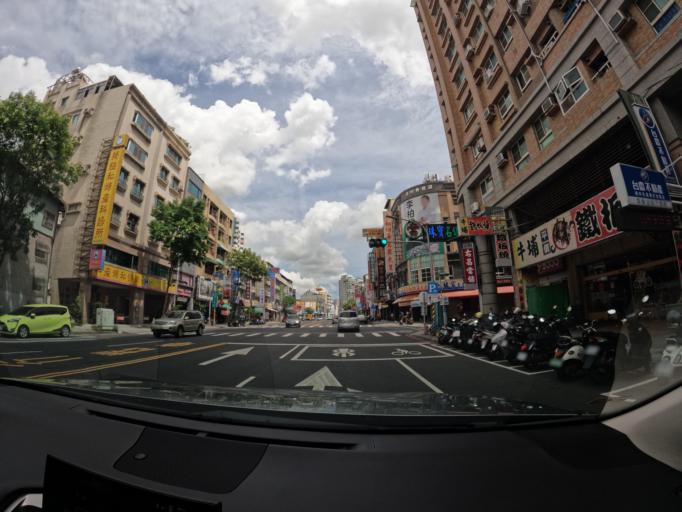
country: TW
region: Kaohsiung
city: Kaohsiung
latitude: 22.7117
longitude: 120.2920
